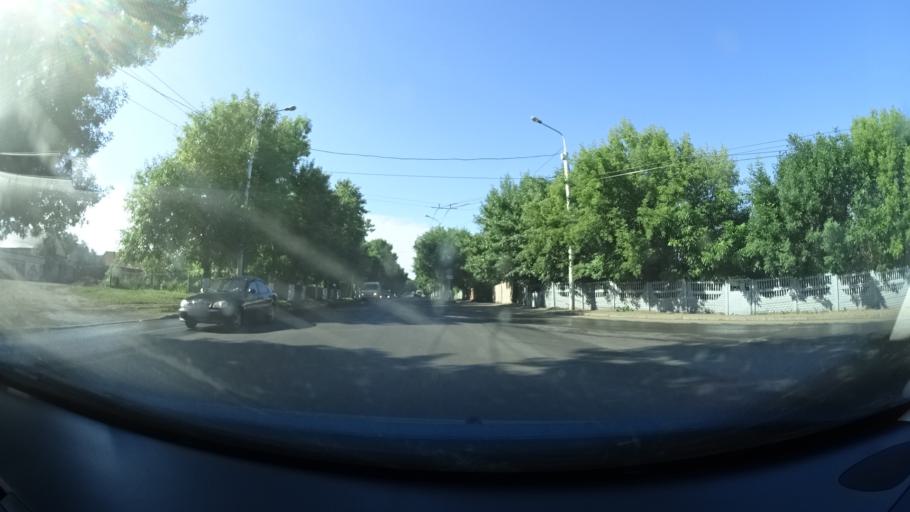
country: RU
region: Bashkortostan
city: Ufa
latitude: 54.8291
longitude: 56.0652
